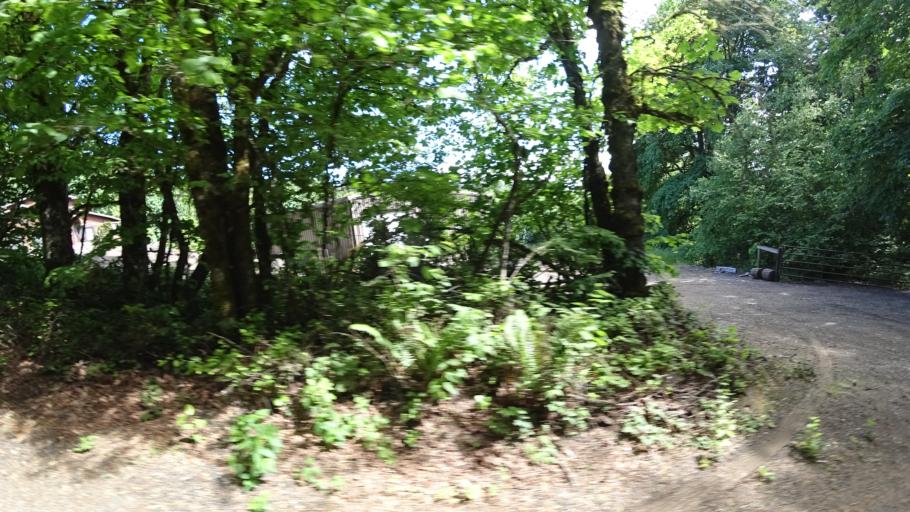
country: US
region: Oregon
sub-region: Washington County
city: Oak Hills
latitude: 45.5789
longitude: -122.8018
